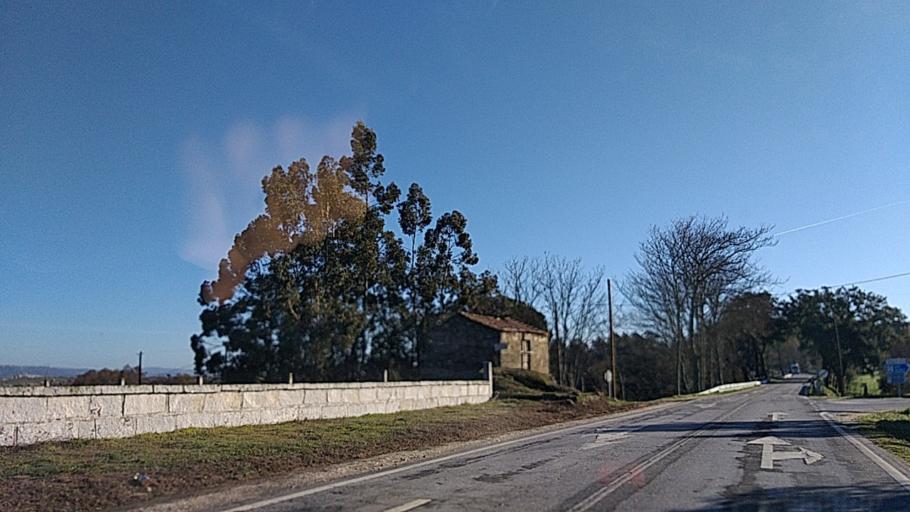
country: PT
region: Guarda
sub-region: Fornos de Algodres
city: Fornos de Algodres
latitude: 40.5216
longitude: -7.6142
